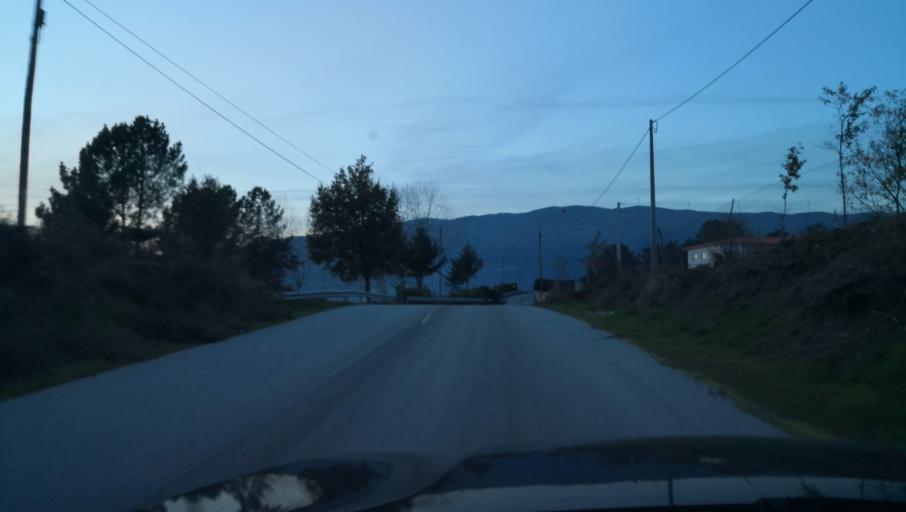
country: PT
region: Vila Real
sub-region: Vila Real
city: Vila Real
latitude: 41.3391
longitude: -7.7028
